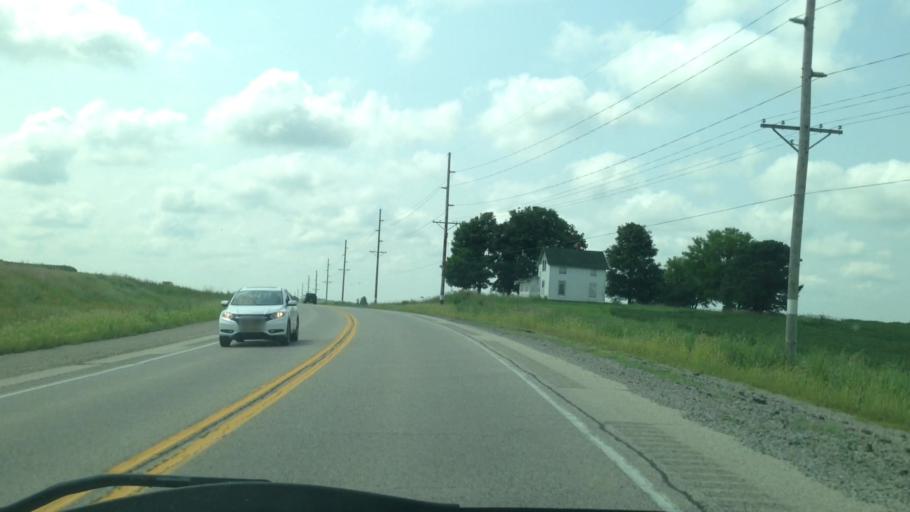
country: US
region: Iowa
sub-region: Benton County
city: Walford
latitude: 41.8725
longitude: -91.8702
